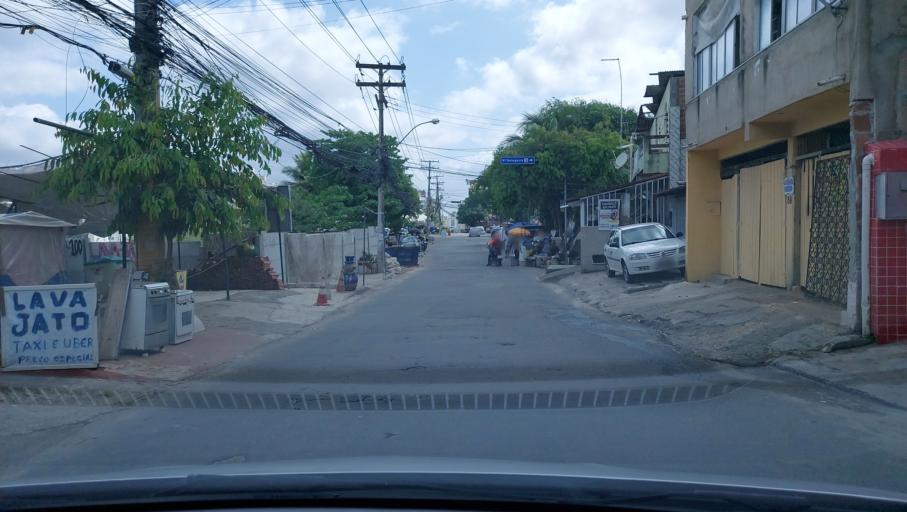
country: BR
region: Bahia
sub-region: Salvador
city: Salvador
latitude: -12.9765
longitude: -38.4376
